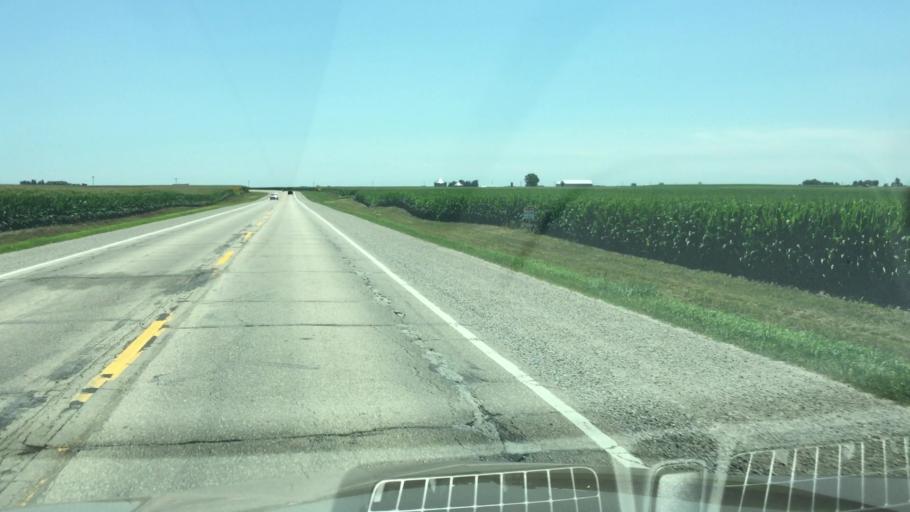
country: US
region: Iowa
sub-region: Cedar County
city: Mechanicsville
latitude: 41.8918
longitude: -91.2175
